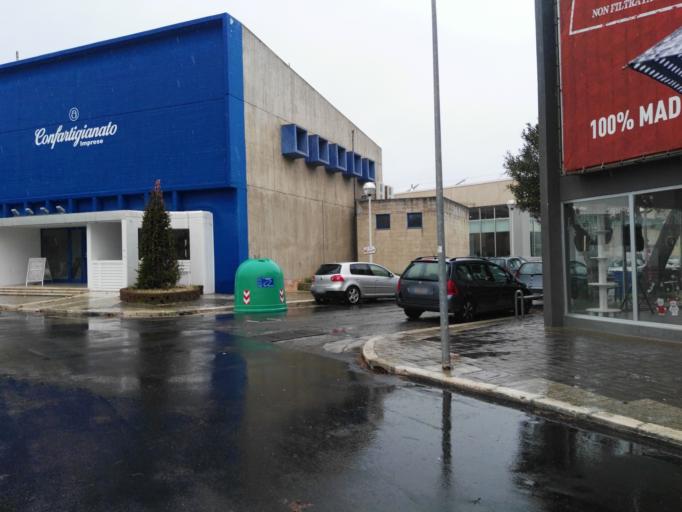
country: IT
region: Apulia
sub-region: Provincia di Bari
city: Bari
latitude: 41.1367
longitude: 16.8381
